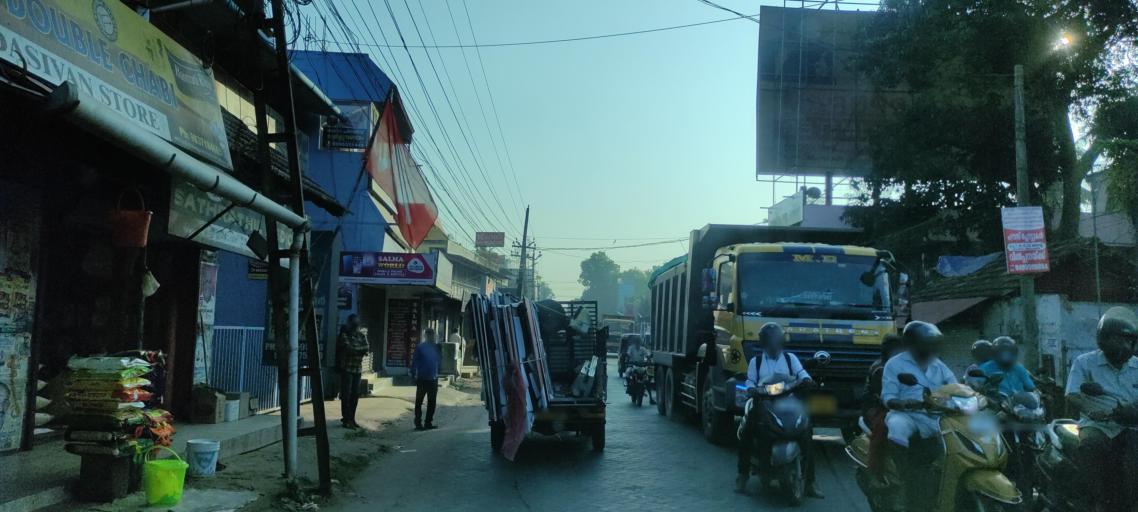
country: IN
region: Kerala
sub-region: Alappuzha
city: Kattanam
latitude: 9.1771
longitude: 76.5272
